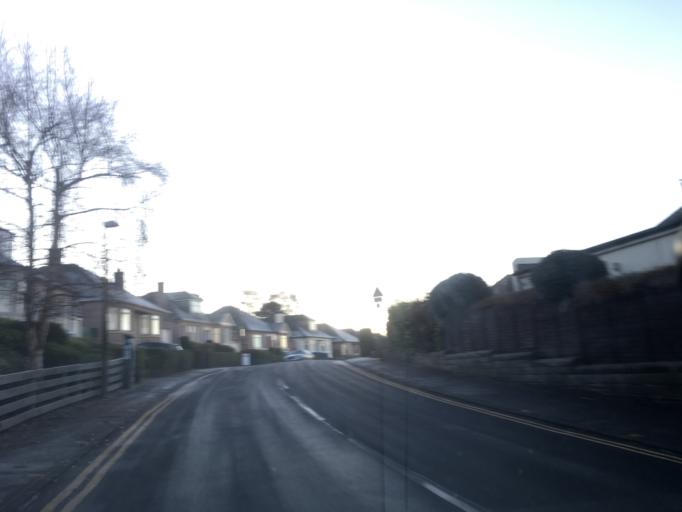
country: GB
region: Scotland
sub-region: Edinburgh
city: Edinburgh
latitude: 55.9540
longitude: -3.2301
